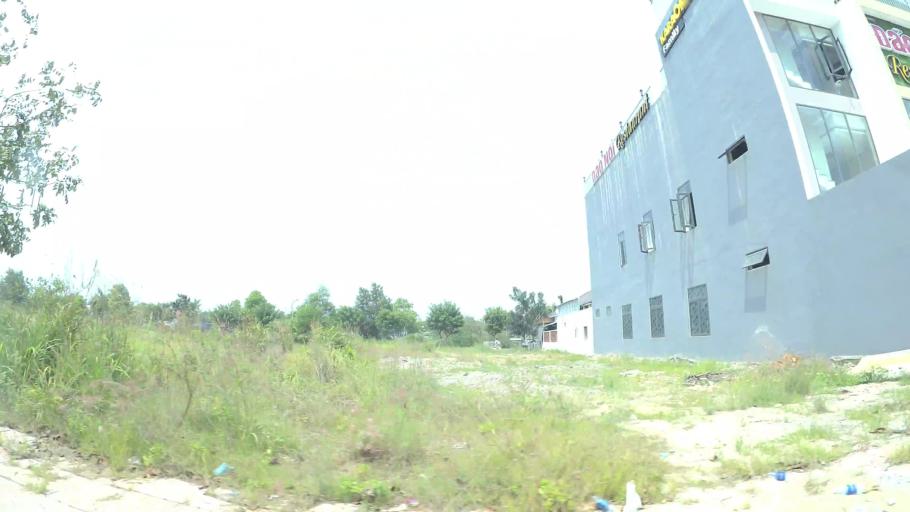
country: VN
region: Da Nang
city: Cam Le
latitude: 16.0162
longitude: 108.2123
